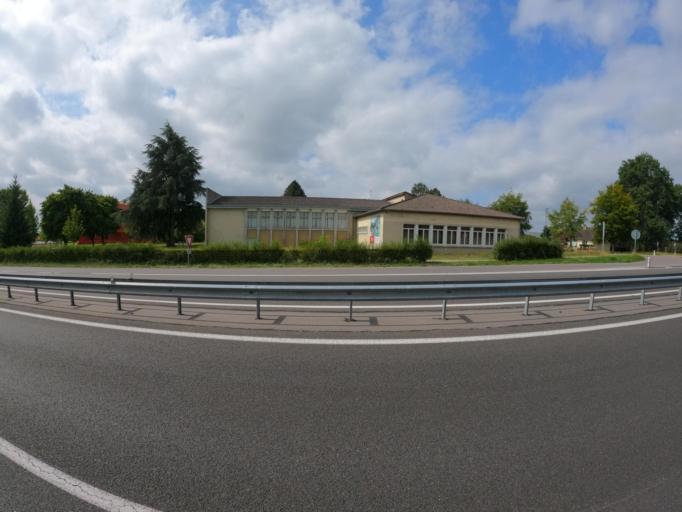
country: FR
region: Limousin
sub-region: Departement de la Haute-Vienne
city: Isle
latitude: 45.8434
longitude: 1.1777
